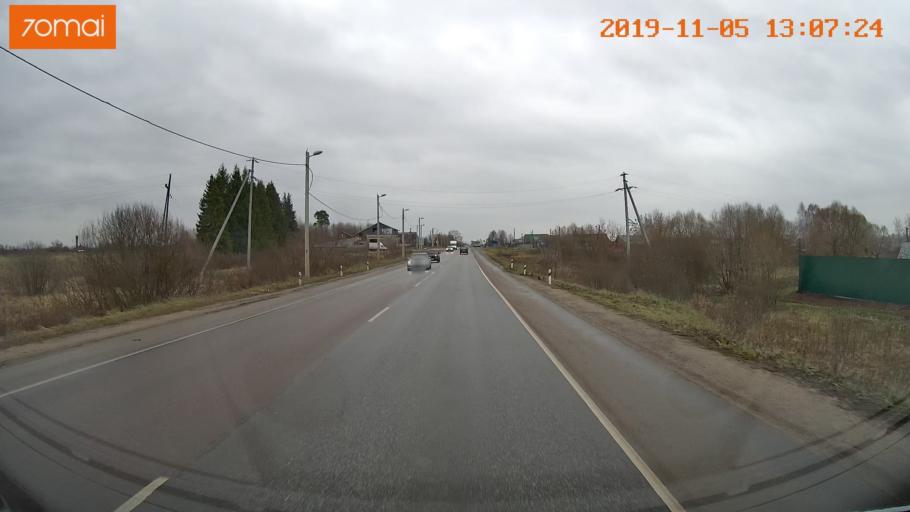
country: RU
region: Ivanovo
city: Kitovo
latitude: 56.8681
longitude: 41.2798
